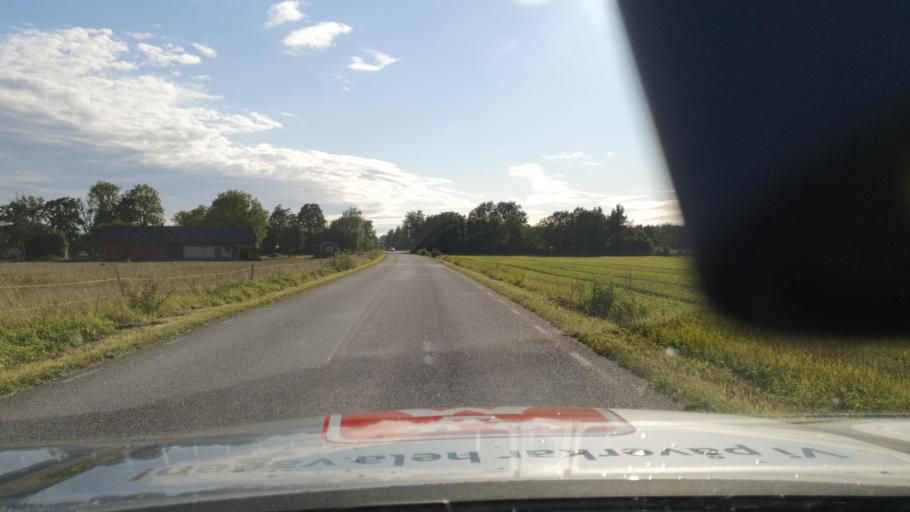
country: SE
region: Gotland
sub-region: Gotland
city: Visby
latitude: 57.5584
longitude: 18.5479
